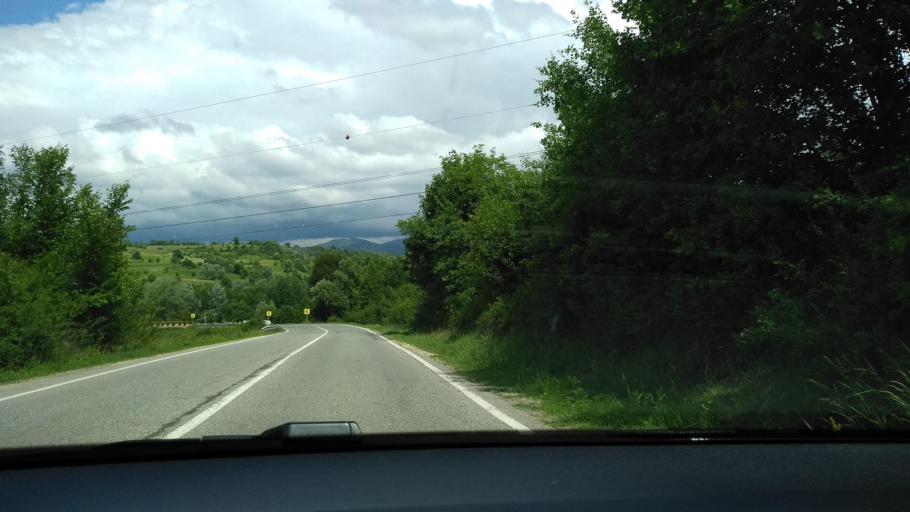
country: RO
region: Gorj
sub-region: Comuna Baia de Fier
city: Baia de Fier
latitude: 45.1530
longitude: 23.7935
